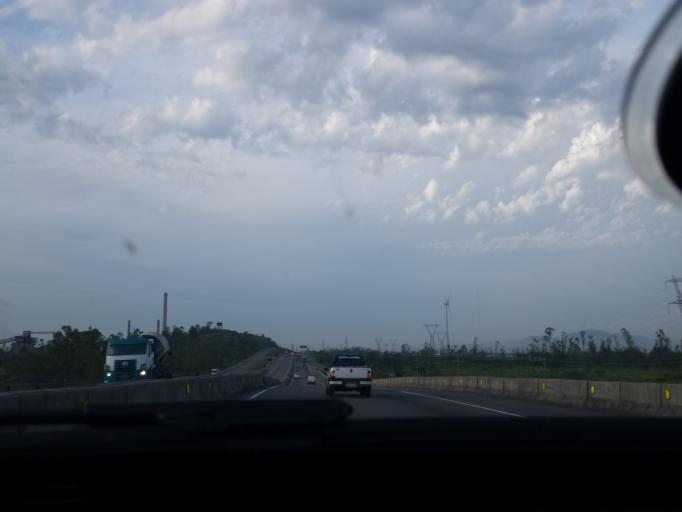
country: BR
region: Santa Catarina
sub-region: Tubarao
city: Tubarao
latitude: -28.4398
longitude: -48.9628
